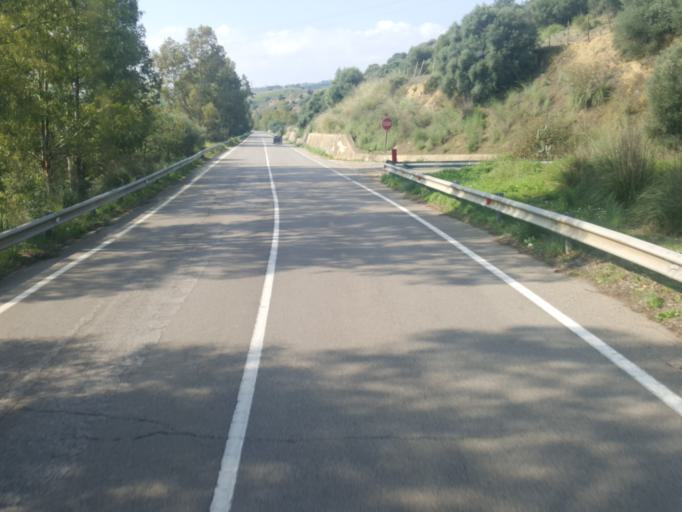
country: IT
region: Sicily
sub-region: Enna
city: Villarosa
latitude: 37.5029
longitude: 14.1595
